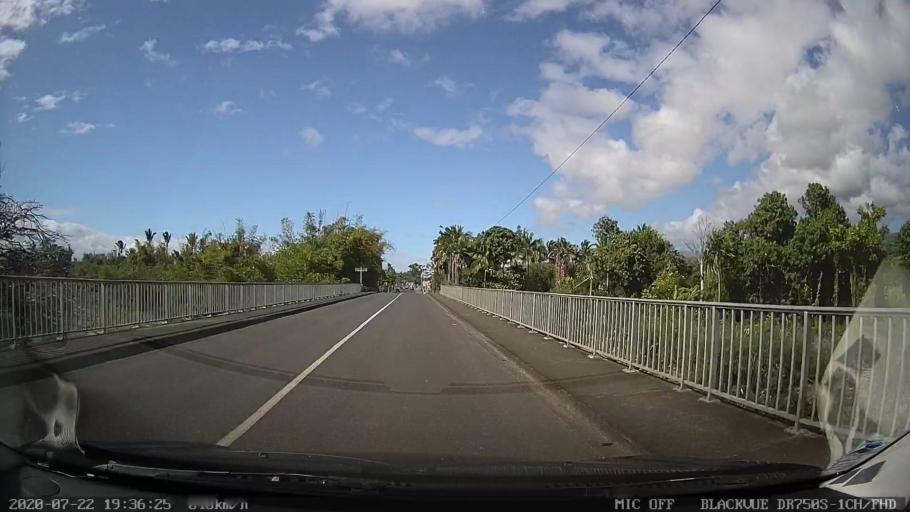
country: RE
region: Reunion
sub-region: Reunion
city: Sainte-Suzanne
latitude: -20.9076
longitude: 55.6085
